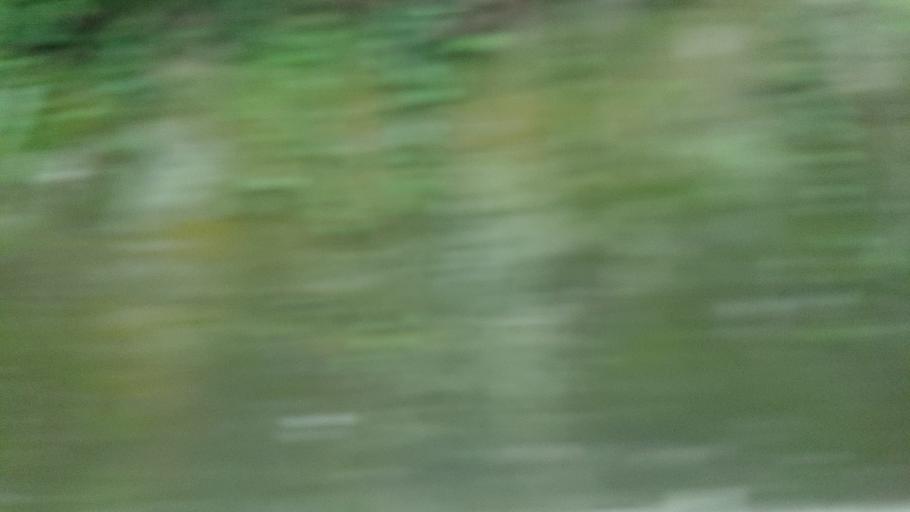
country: TW
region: Taiwan
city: Daxi
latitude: 24.8919
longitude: 121.3760
